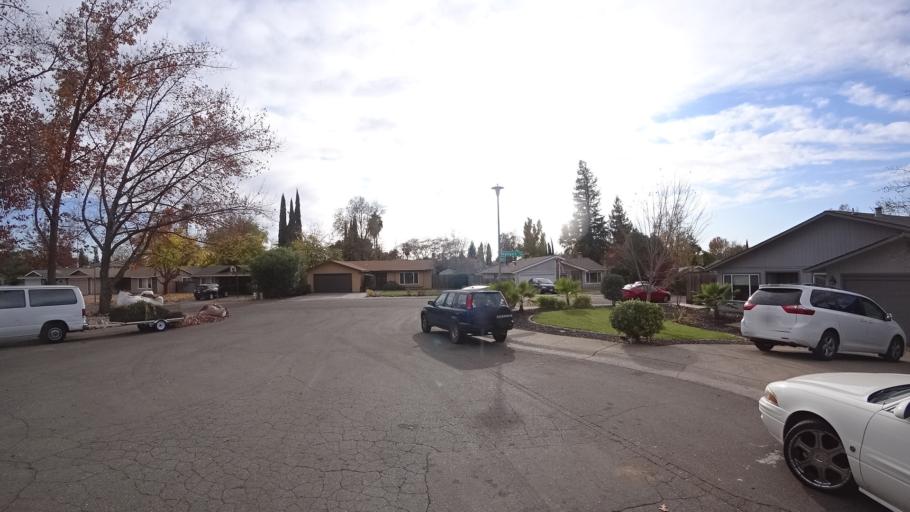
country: US
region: California
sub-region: Sacramento County
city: Citrus Heights
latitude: 38.7075
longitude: -121.2521
